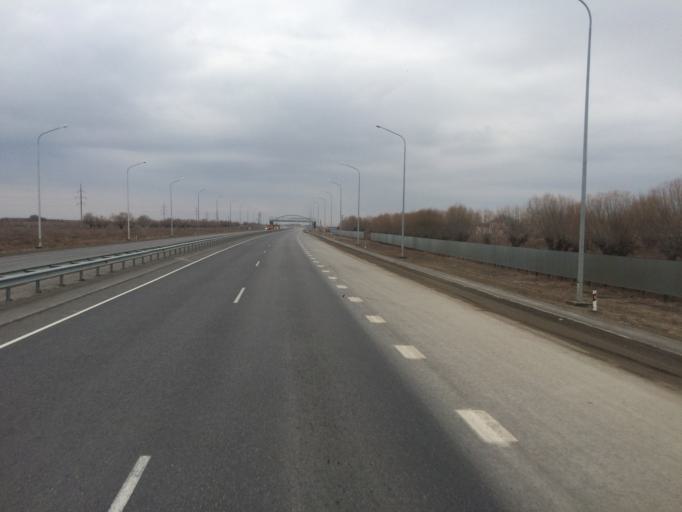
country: KZ
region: Qyzylorda
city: Shieli
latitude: 44.1350
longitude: 66.9732
